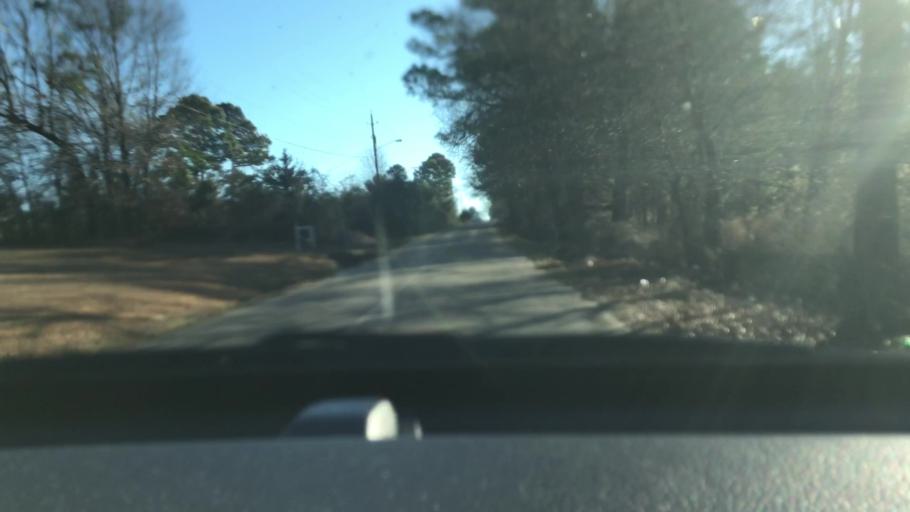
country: US
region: Arkansas
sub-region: Hempstead County
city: Hope
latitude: 33.6390
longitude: -93.5826
